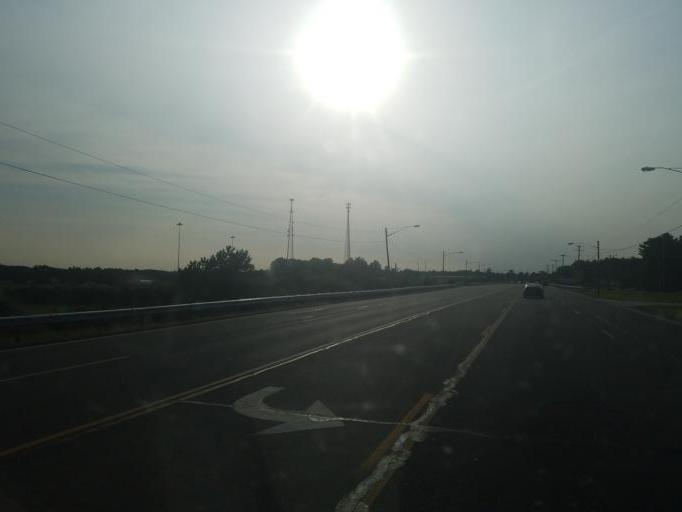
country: US
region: Ohio
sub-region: Richland County
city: Ontario
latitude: 40.7742
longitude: -82.6046
